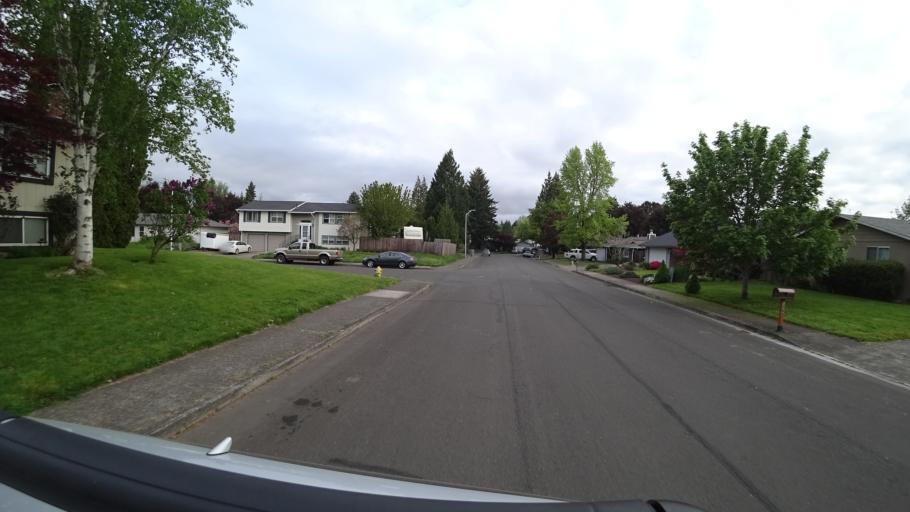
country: US
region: Oregon
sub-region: Washington County
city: Aloha
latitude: 45.5061
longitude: -122.9268
